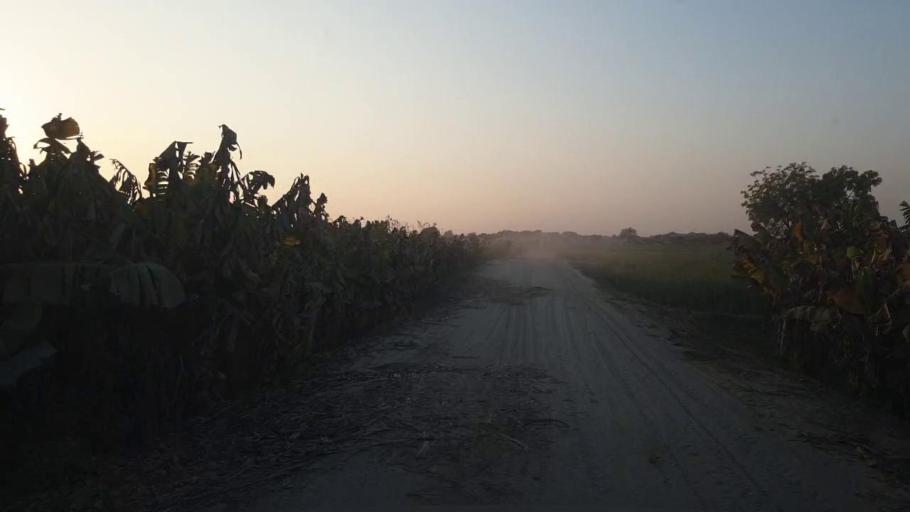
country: PK
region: Sindh
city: Bhit Shah
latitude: 25.8192
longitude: 68.5025
